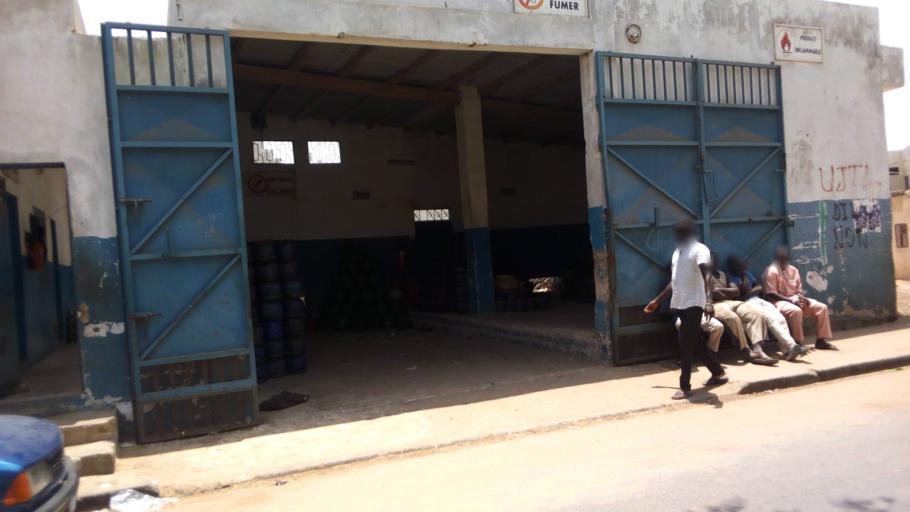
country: SN
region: Dakar
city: Pikine
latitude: 14.7810
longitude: -17.3756
